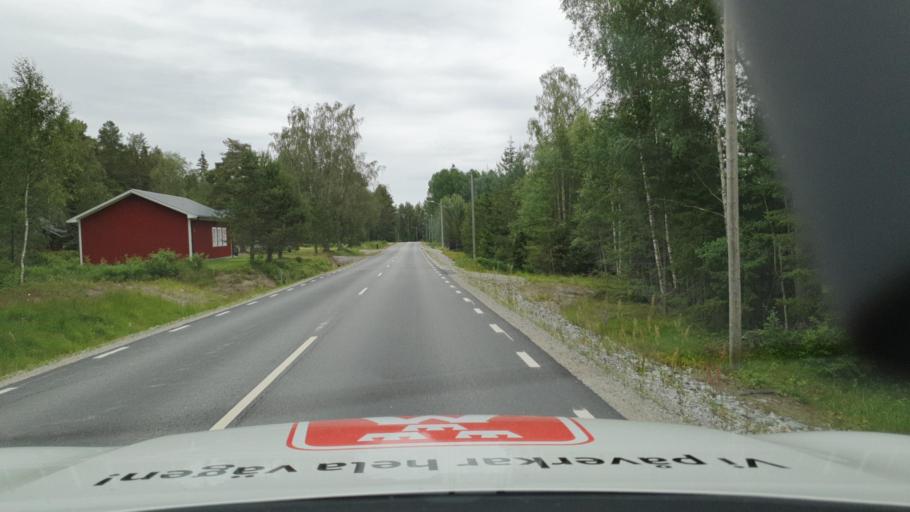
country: SE
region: Vaesterbotten
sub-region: Nordmalings Kommun
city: Nordmaling
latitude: 63.5270
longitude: 19.3626
